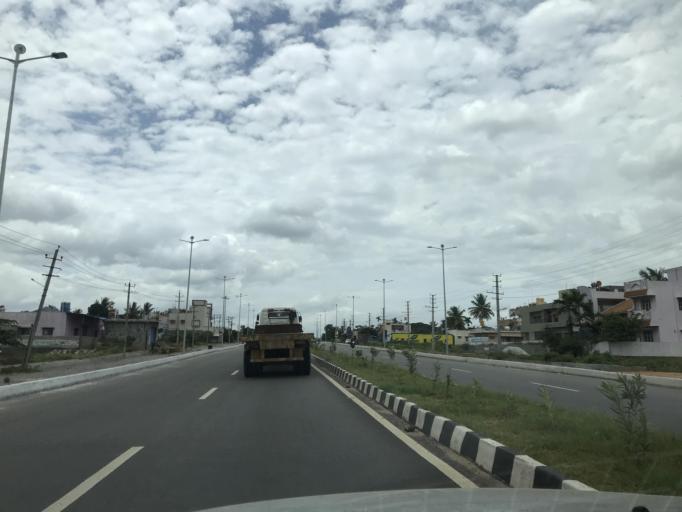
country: IN
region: Karnataka
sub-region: Tumkur
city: Tumkur
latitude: 13.3093
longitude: 77.1389
